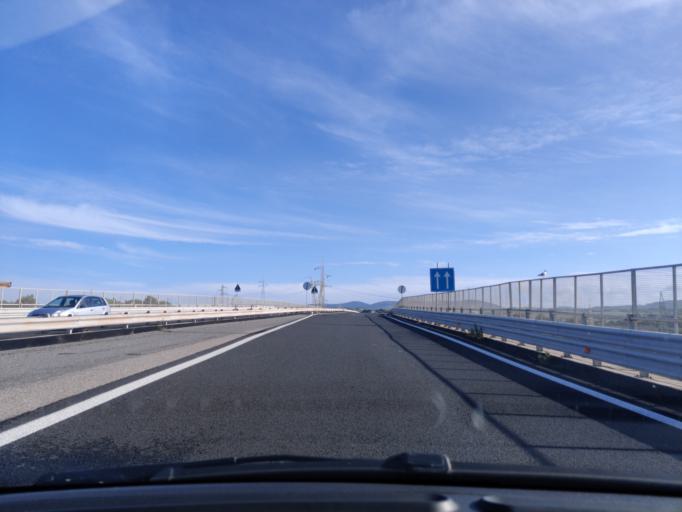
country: IT
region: Latium
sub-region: Citta metropolitana di Roma Capitale
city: Civitavecchia
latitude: 42.1036
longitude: 11.7854
